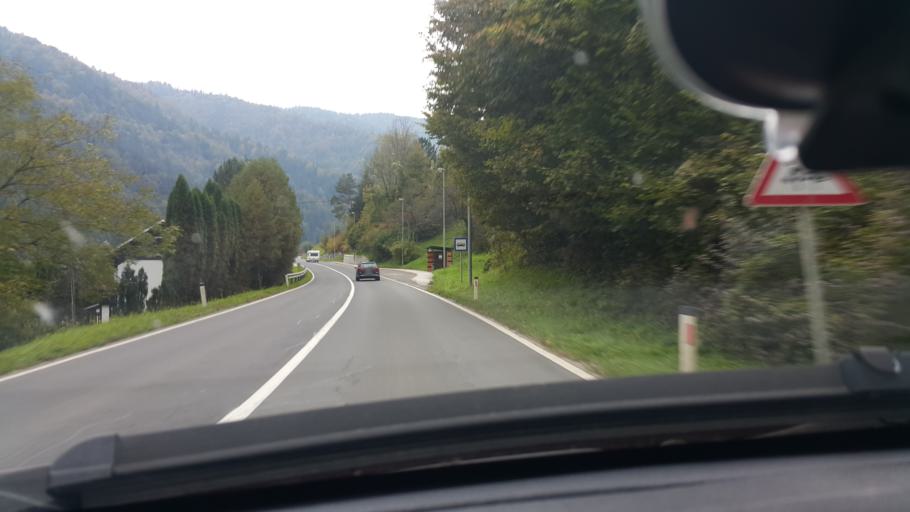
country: SI
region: Podvelka
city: Podvelka
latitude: 46.5847
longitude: 15.3687
